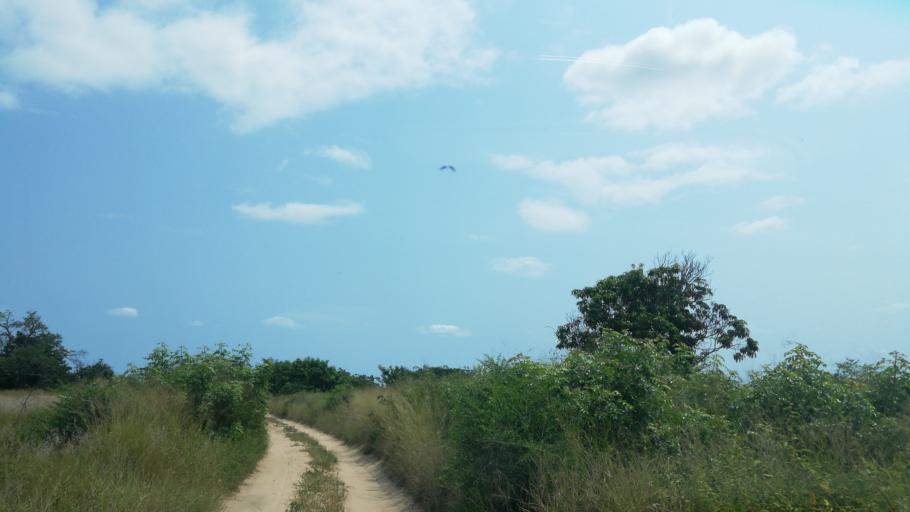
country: MZ
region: Maputo
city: Matola
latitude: -26.1102
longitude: 32.4228
